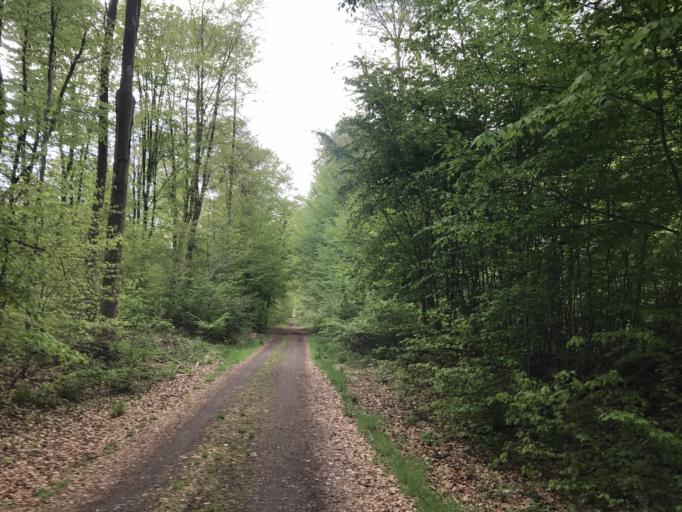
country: DE
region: Hesse
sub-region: Regierungsbezirk Giessen
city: Hungen
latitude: 50.5020
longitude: 8.9145
